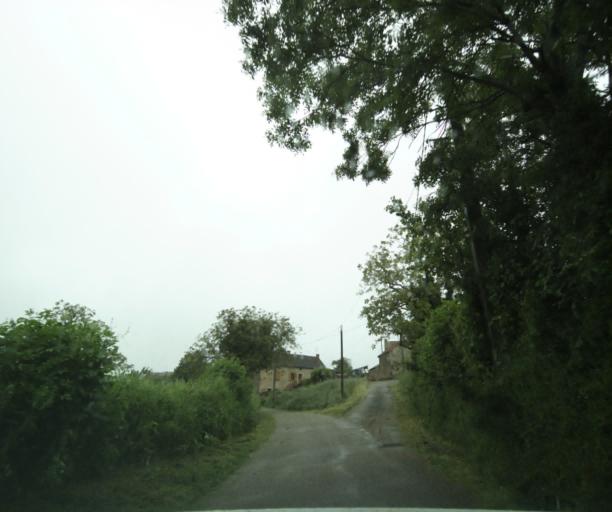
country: FR
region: Bourgogne
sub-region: Departement de Saone-et-Loire
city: Charolles
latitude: 46.4101
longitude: 4.3879
